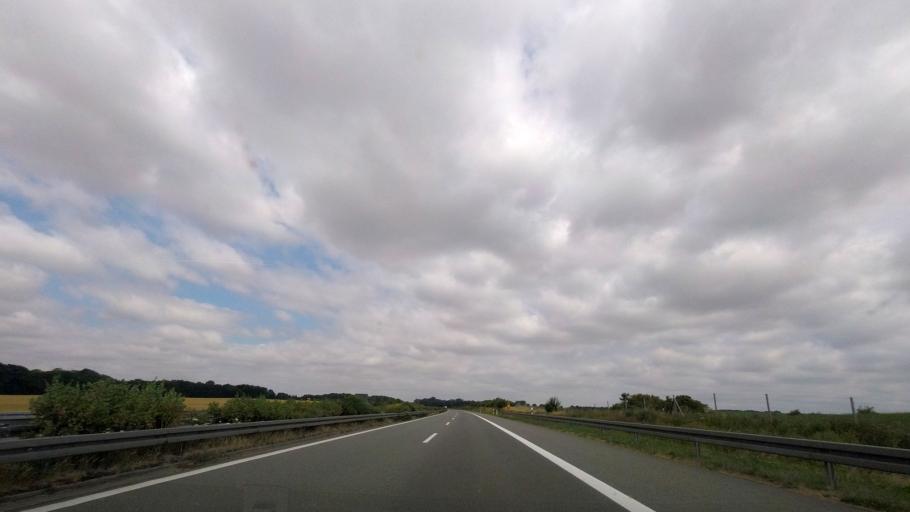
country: DE
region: Mecklenburg-Vorpommern
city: Jarmen
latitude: 53.9662
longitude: 13.3654
